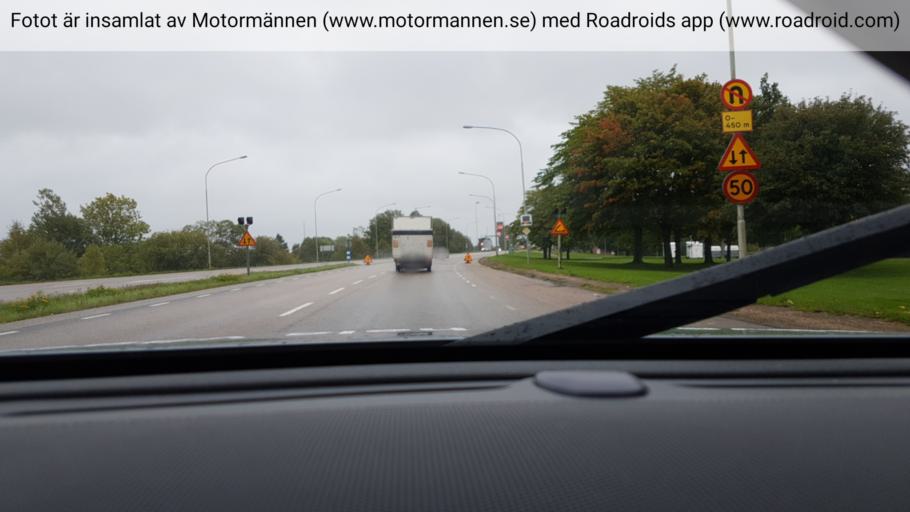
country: SE
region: Vaestra Goetaland
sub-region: Vanersborgs Kommun
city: Vanersborg
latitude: 58.3633
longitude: 12.3149
